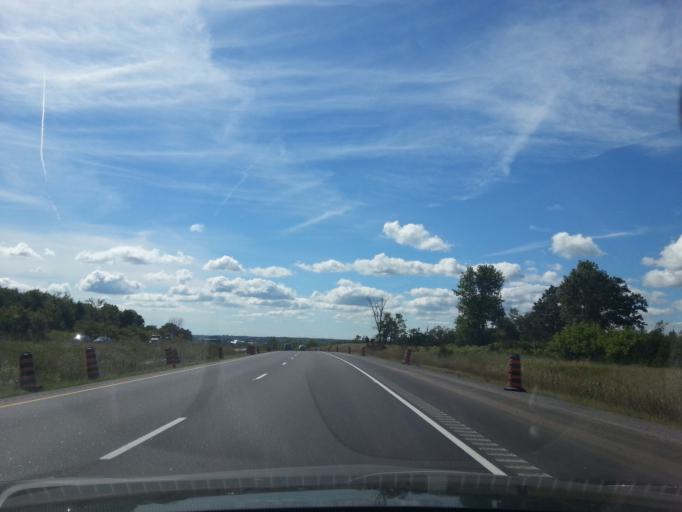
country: CA
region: Ontario
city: Skatepark
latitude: 44.2727
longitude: -76.9125
